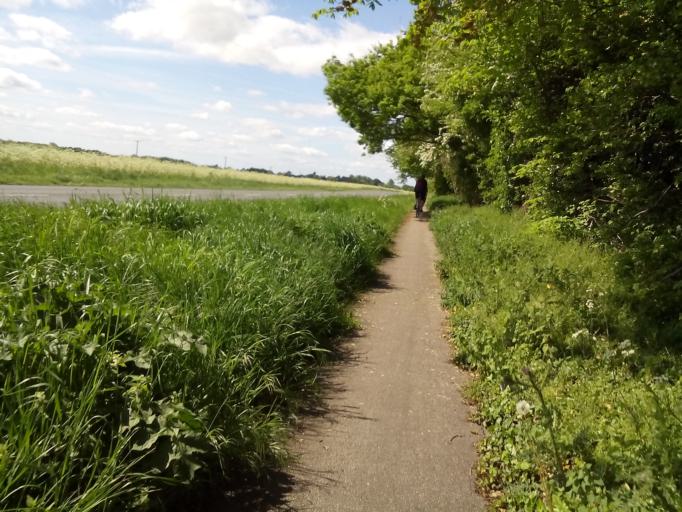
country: GB
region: England
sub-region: Cambridgeshire
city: Harston
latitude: 52.1280
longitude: 0.0651
